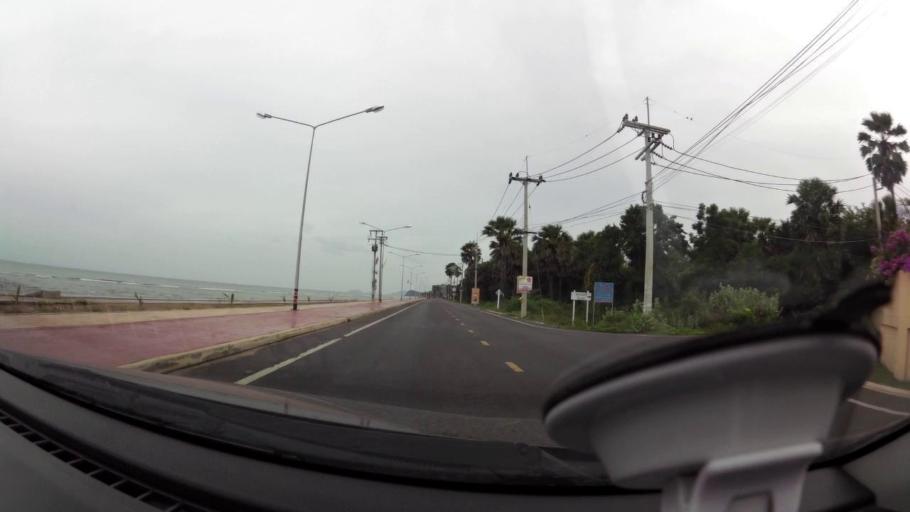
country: TH
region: Prachuap Khiri Khan
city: Pran Buri
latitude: 12.3768
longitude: 100.0002
